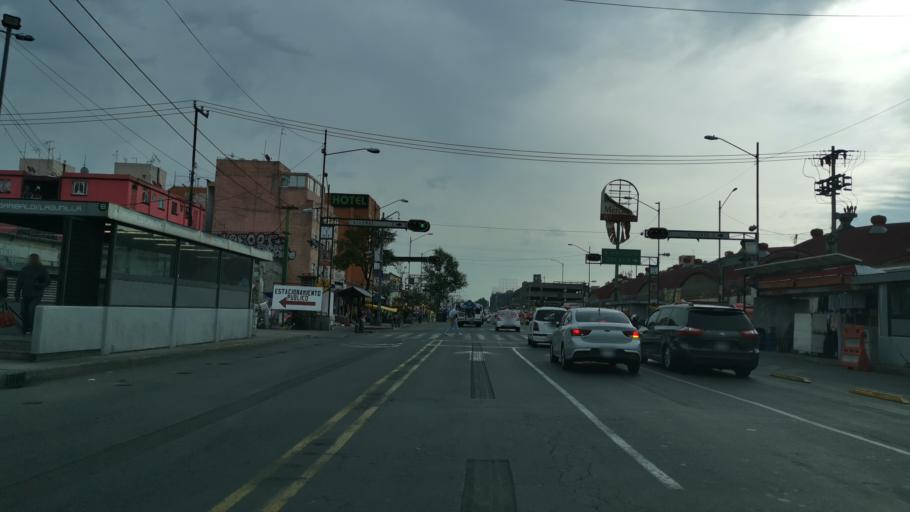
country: MX
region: Mexico City
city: Cuauhtemoc
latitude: 19.4439
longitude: -99.1374
